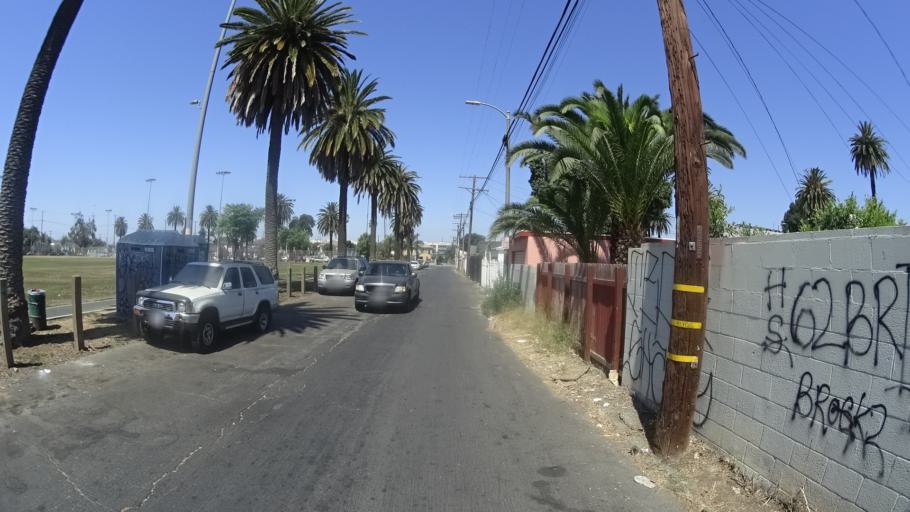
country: US
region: California
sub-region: Los Angeles County
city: Westmont
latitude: 33.9846
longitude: -118.3054
